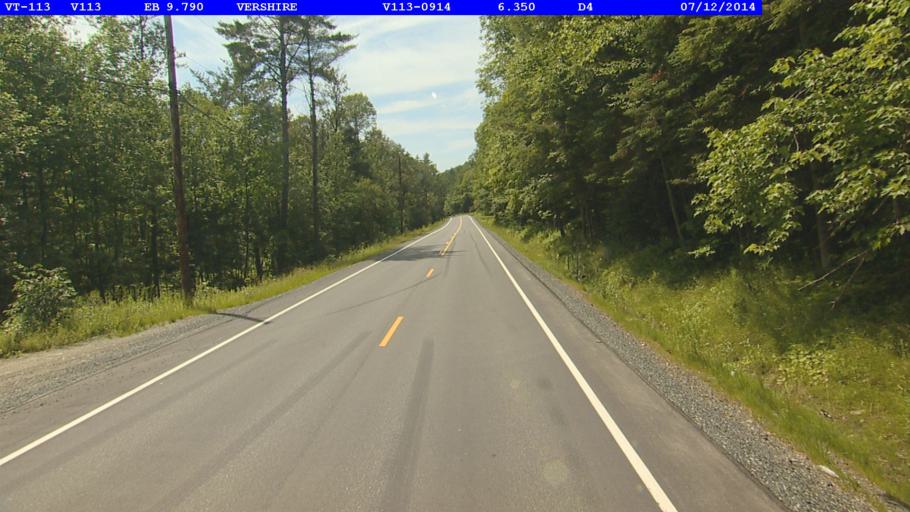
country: US
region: New Hampshire
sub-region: Grafton County
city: Orford
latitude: 43.9537
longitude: -72.2775
